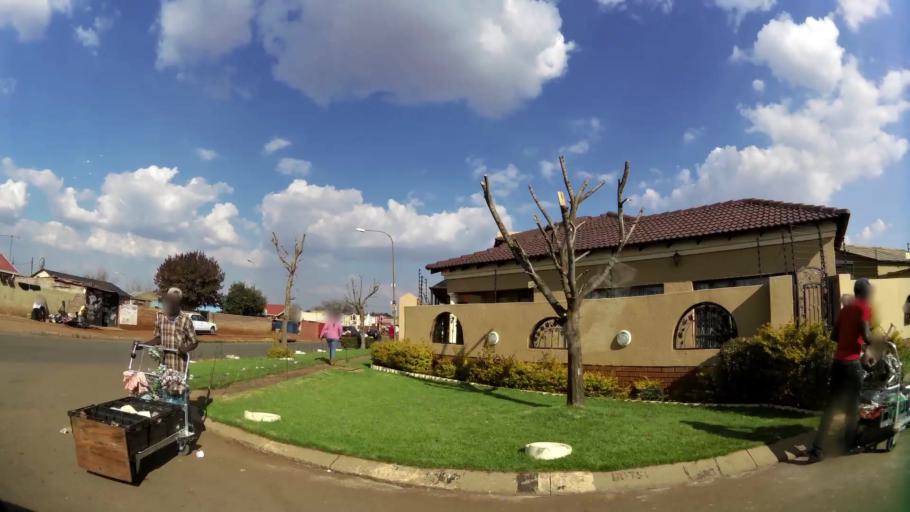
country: ZA
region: Gauteng
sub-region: City of Johannesburg Metropolitan Municipality
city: Soweto
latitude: -26.2222
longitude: 27.8684
